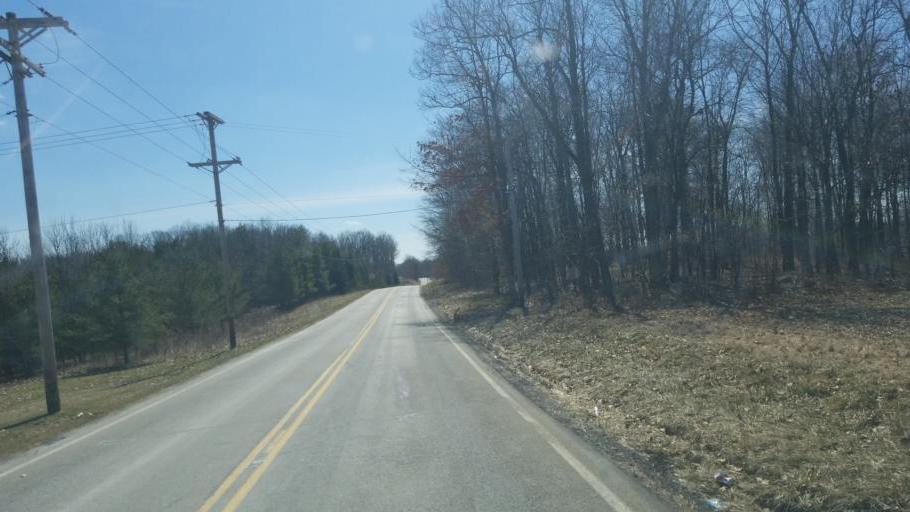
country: US
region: Ohio
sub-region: Knox County
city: Oak Hill
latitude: 40.4620
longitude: -82.1298
